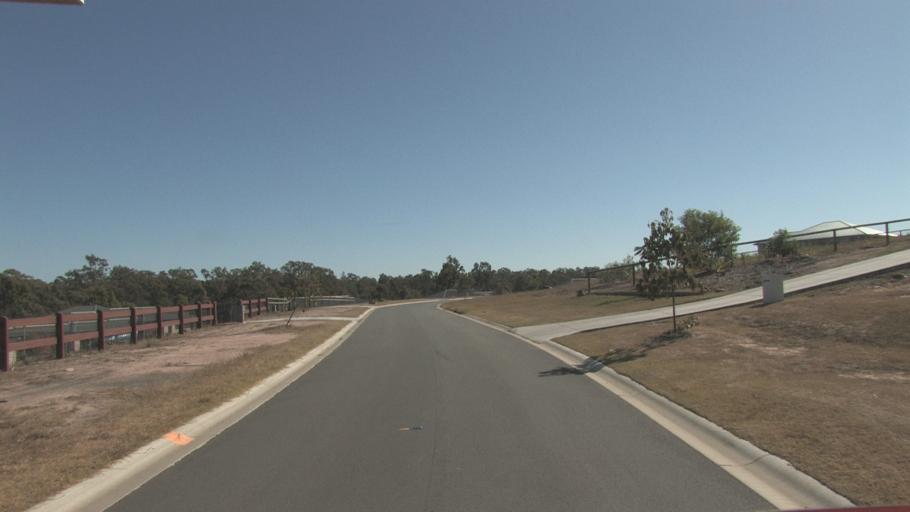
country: AU
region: Queensland
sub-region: Logan
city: Cedar Vale
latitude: -27.8635
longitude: 153.0433
